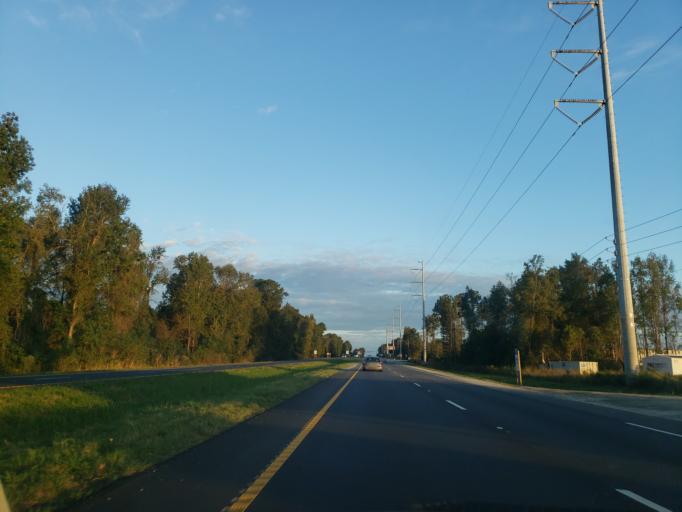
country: US
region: Georgia
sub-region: Chatham County
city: Port Wentworth
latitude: 32.1402
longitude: -81.1753
